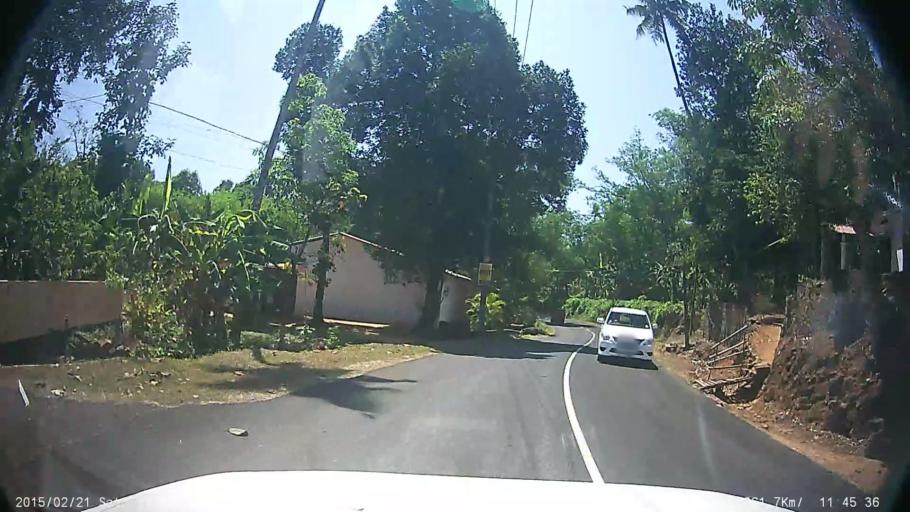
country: IN
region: Kerala
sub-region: Kottayam
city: Lalam
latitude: 9.7797
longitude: 76.7229
